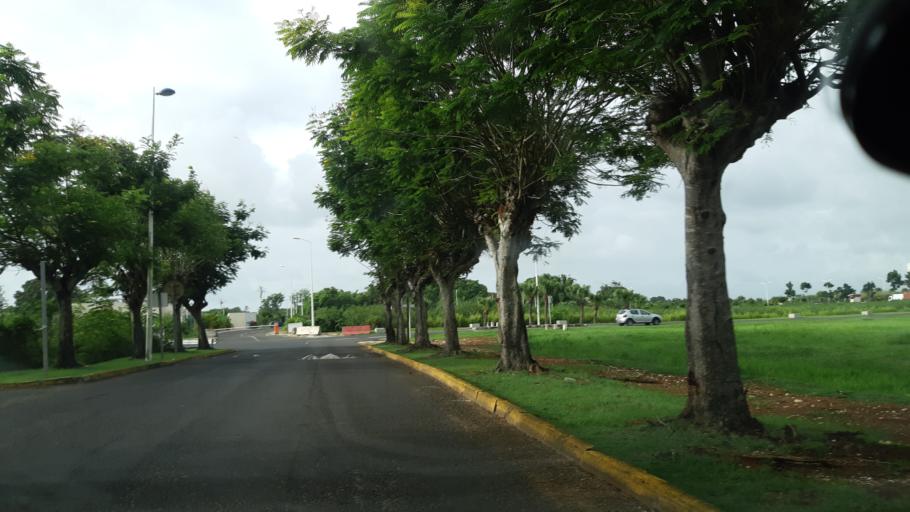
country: GP
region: Guadeloupe
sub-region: Guadeloupe
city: Les Abymes
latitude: 16.2710
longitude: -61.5222
